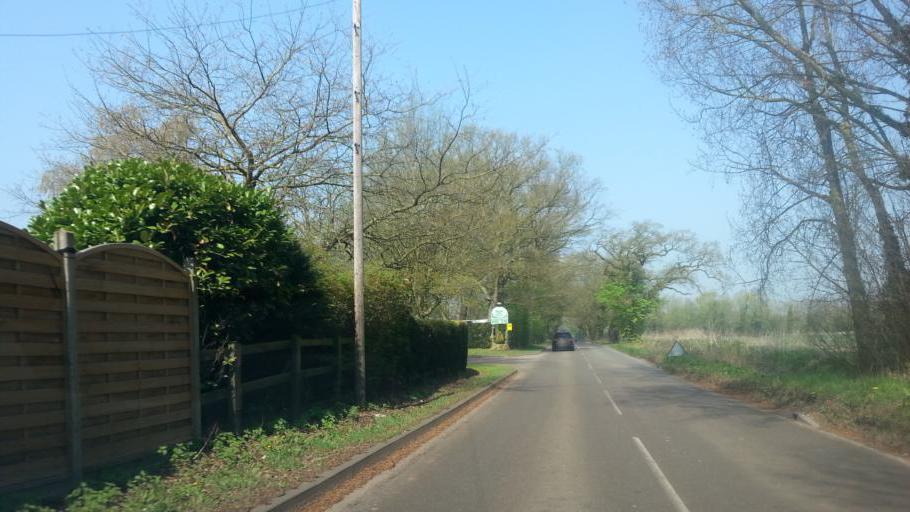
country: GB
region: England
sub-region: Suffolk
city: Thurston
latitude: 52.2406
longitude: 0.8244
